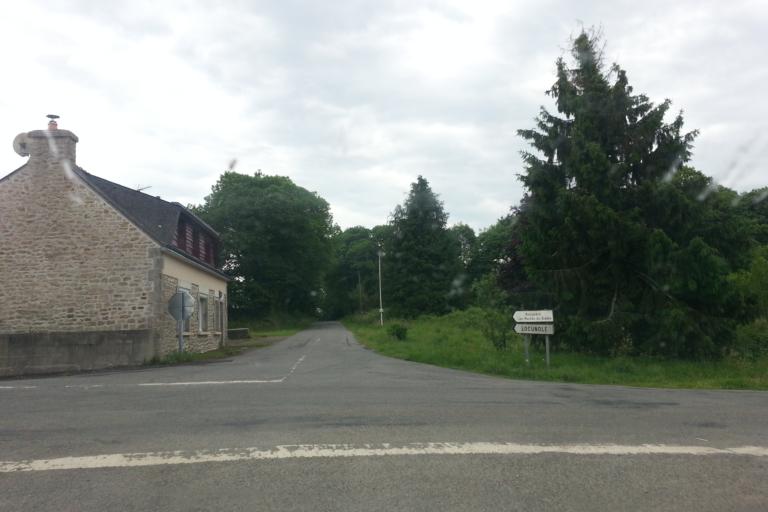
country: FR
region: Brittany
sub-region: Departement du Morbihan
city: Meslan
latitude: 47.9888
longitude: -3.4565
